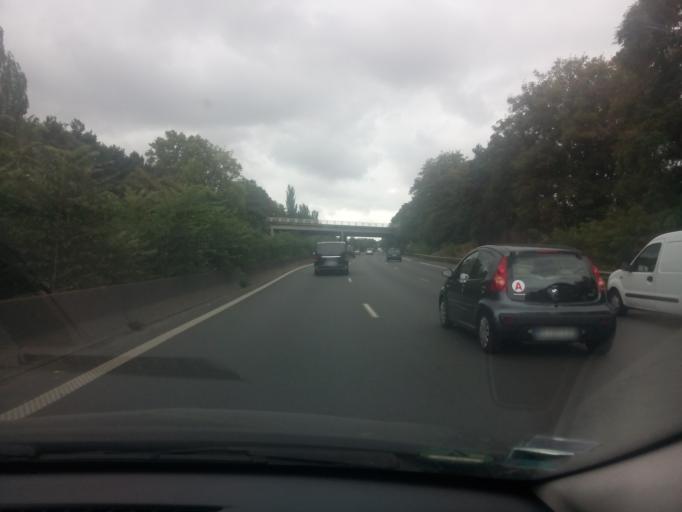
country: FR
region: Ile-de-France
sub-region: Departement du Val-de-Marne
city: Gentilly
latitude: 48.8052
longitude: 2.3418
